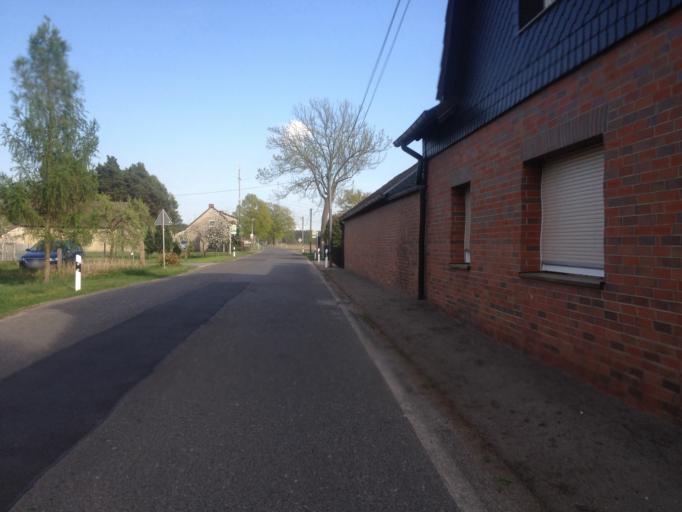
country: DE
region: Brandenburg
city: Drachhausen
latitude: 51.8767
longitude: 14.3152
